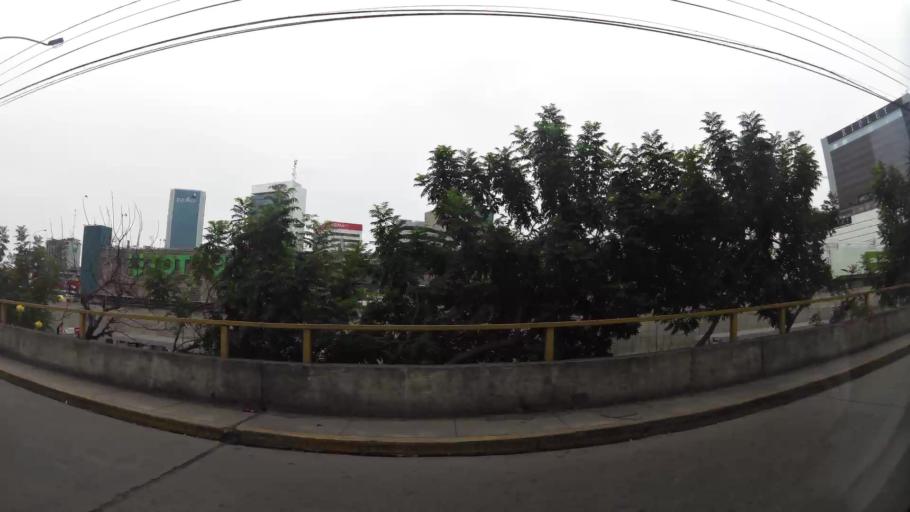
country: PE
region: Lima
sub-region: Lima
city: San Isidro
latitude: -12.0958
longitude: -77.0256
